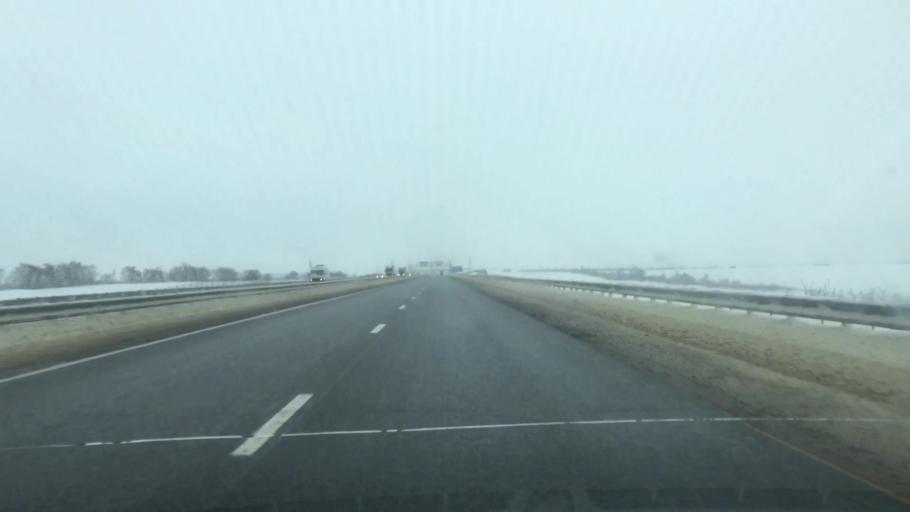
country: RU
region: Tula
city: Yefremov
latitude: 53.2192
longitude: 38.2129
